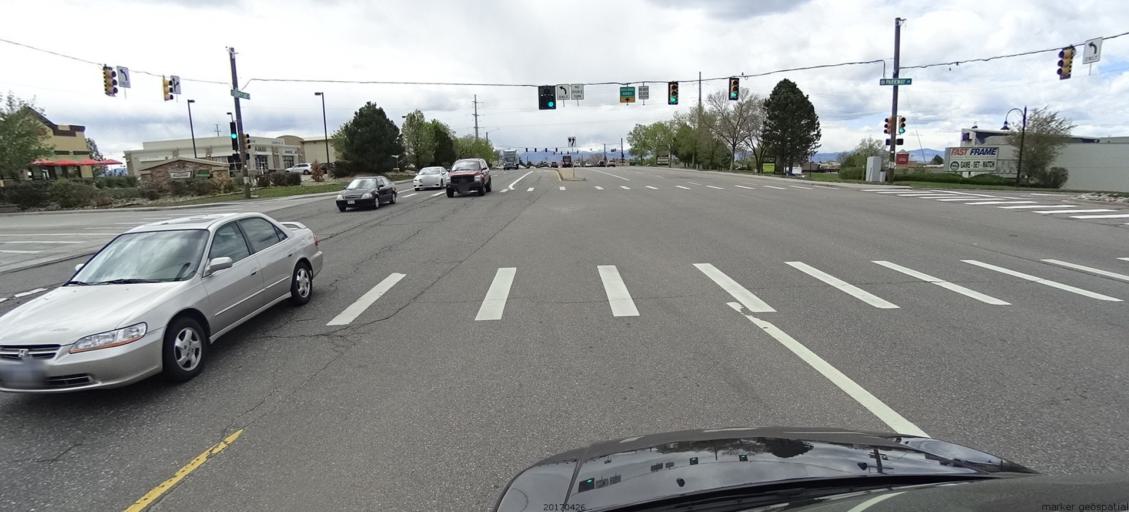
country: US
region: Colorado
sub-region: Douglas County
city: Acres Green
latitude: 39.5660
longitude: -104.9020
